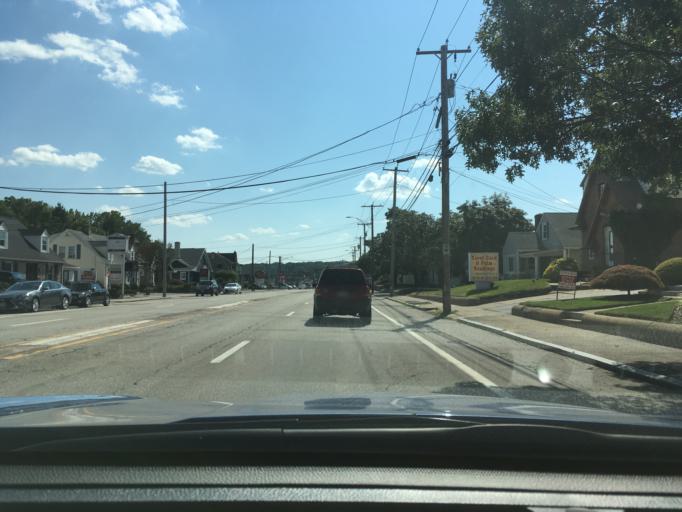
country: US
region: Rhode Island
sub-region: Providence County
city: Cranston
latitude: 41.7768
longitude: -71.4474
